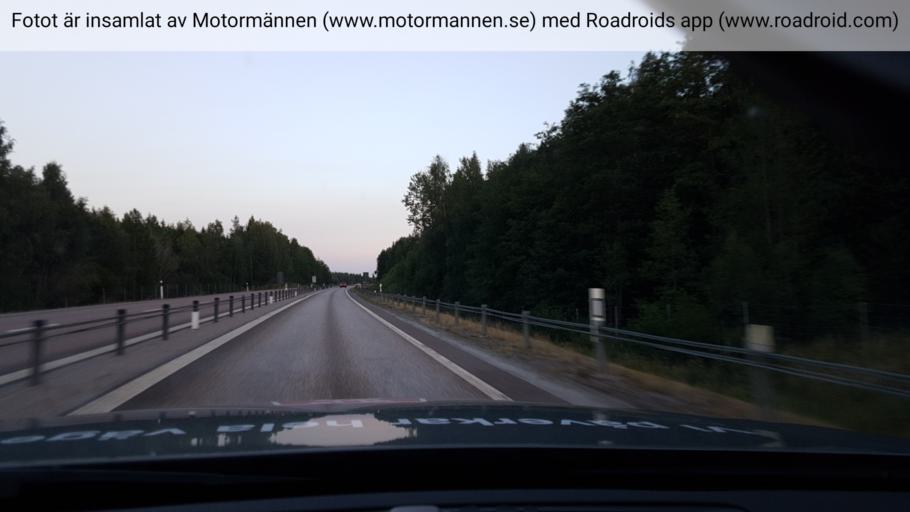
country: SE
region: Vaestmanland
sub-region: Surahammars Kommun
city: Ramnas
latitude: 59.8006
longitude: 16.1442
